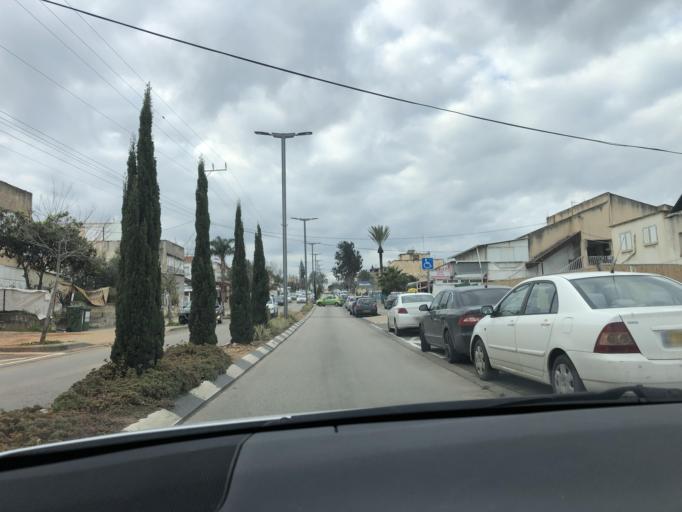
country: IL
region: Central District
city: Rosh Ha'Ayin
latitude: 32.0952
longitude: 34.9544
